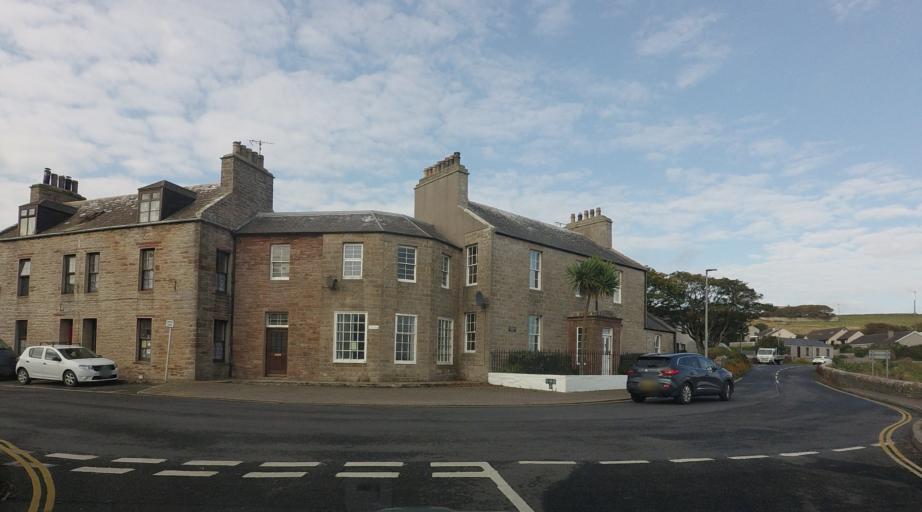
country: GB
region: Scotland
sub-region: Orkney Islands
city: Orkney
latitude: 58.8259
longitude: -2.9609
